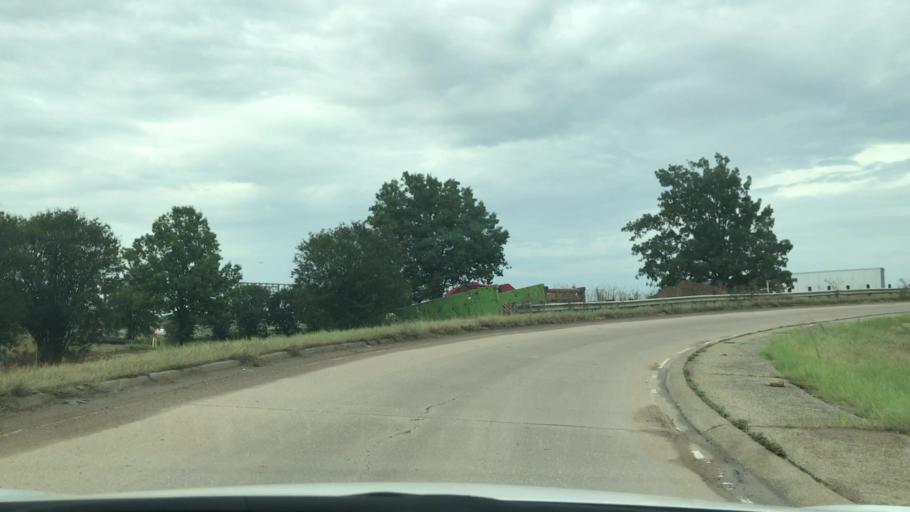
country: US
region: Texas
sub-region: Dallas County
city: Irving
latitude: 32.8392
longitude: -96.9070
